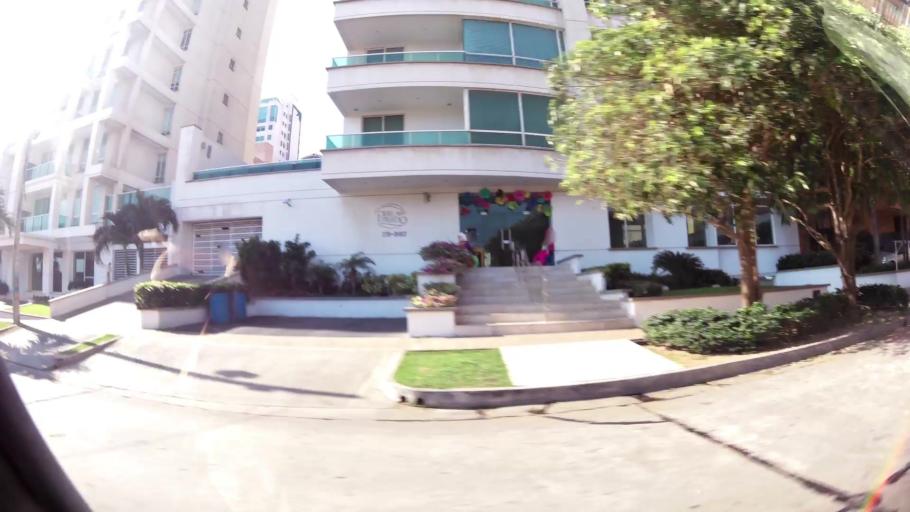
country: CO
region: Atlantico
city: Barranquilla
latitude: 11.0088
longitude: -74.8090
